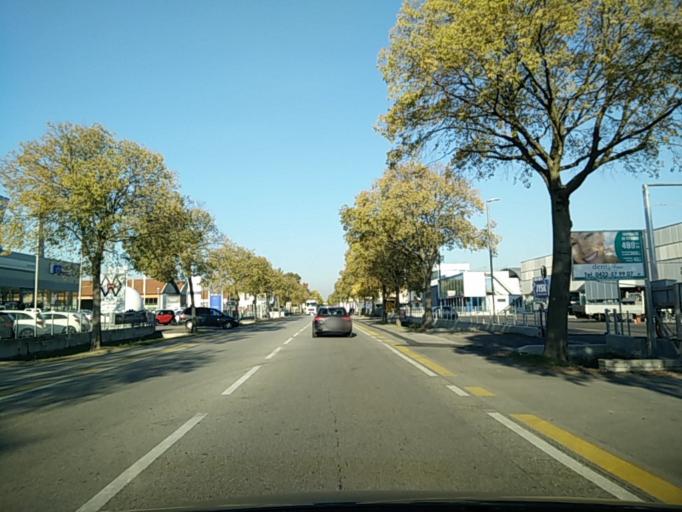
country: IT
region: Veneto
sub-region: Provincia di Treviso
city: Treviso
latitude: 45.6877
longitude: 12.2469
